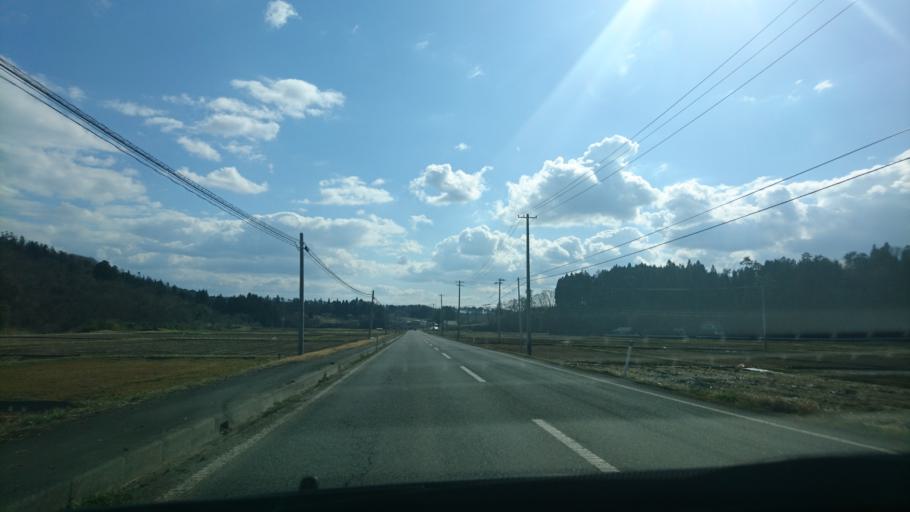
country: JP
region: Iwate
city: Kitakami
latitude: 39.2392
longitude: 141.1982
